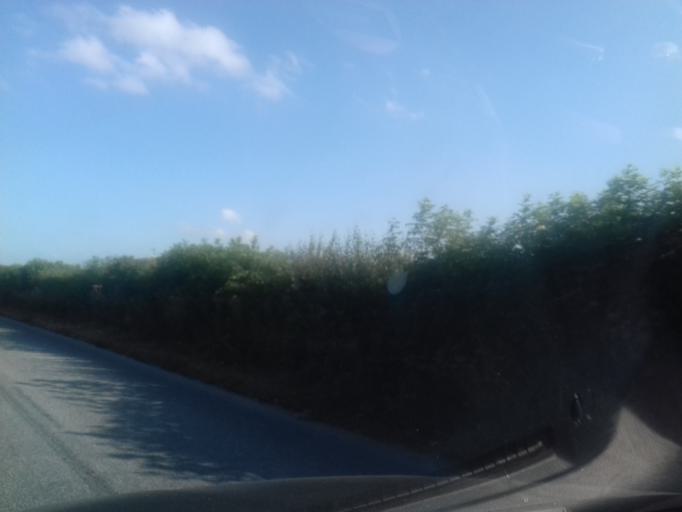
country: IE
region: Leinster
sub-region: Fingal County
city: Blanchardstown
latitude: 53.4464
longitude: -6.3903
